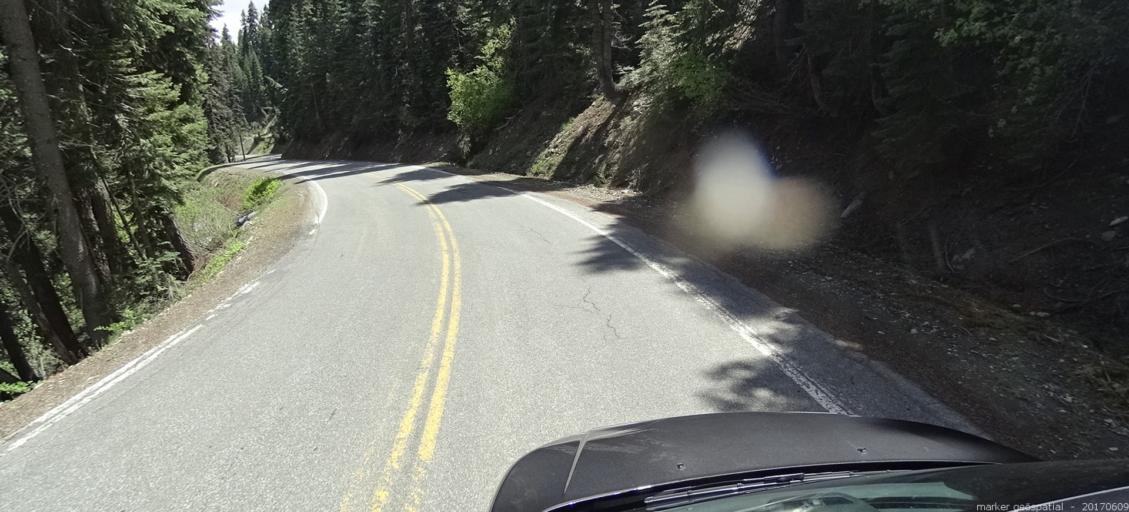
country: US
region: California
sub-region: Siskiyou County
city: Yreka
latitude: 41.4007
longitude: -122.9963
